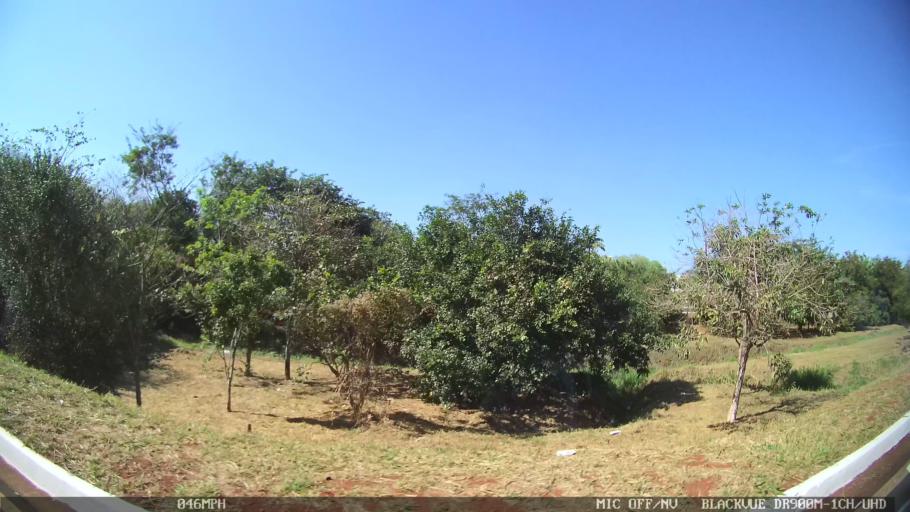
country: BR
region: Sao Paulo
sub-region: Ribeirao Preto
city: Ribeirao Preto
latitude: -21.2345
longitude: -47.7653
